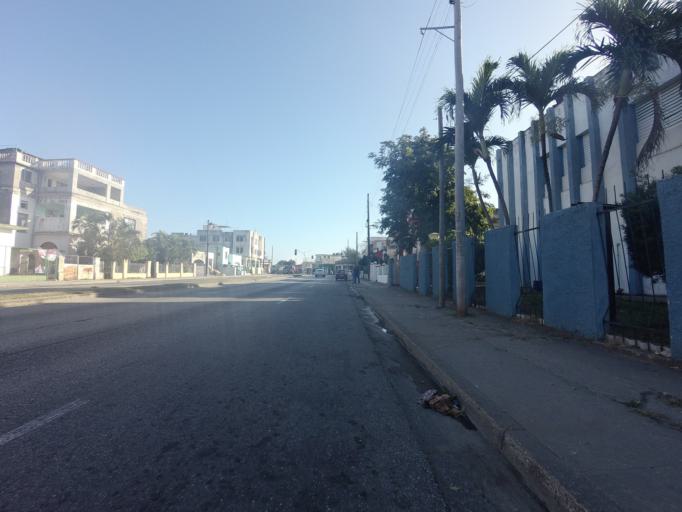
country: CU
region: La Habana
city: Cerro
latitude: 23.1059
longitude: -82.4259
